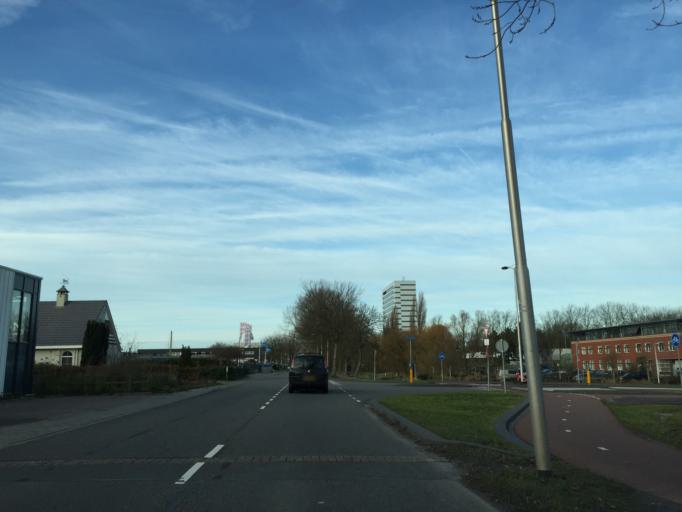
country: NL
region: South Holland
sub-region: Gemeente Delft
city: Delft
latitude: 51.9864
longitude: 4.3766
